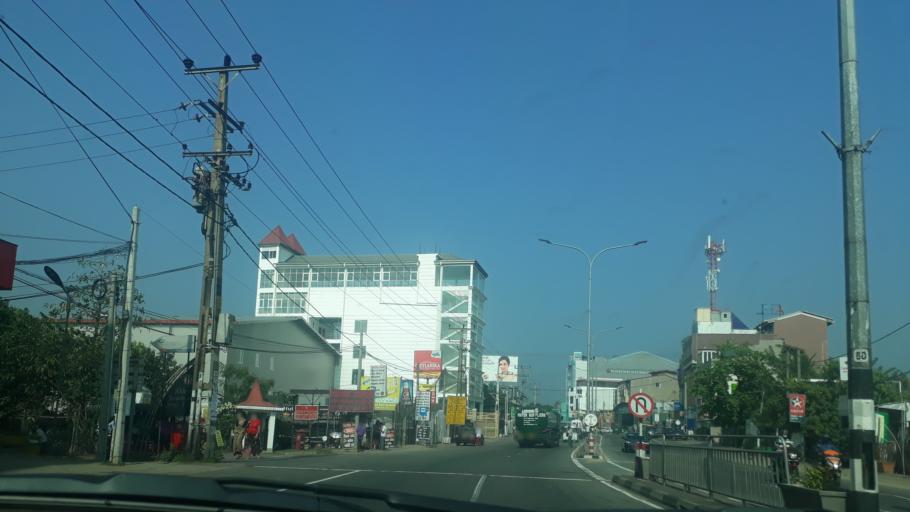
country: LK
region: Western
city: Kelaniya
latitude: 6.9671
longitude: 79.9069
